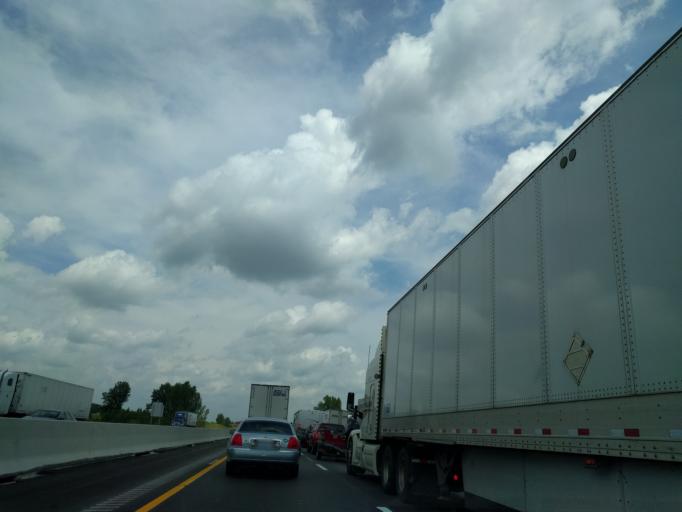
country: US
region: Kentucky
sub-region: Larue County
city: Hodgenville
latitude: 37.5323
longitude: -85.8825
